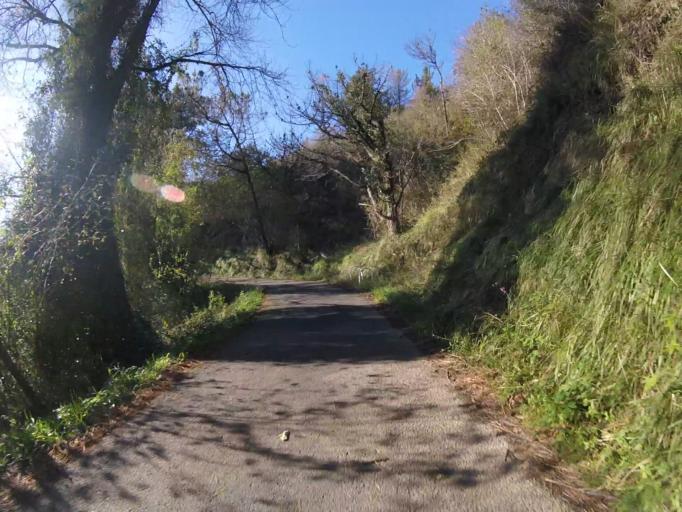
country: ES
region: Basque Country
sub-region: Provincia de Guipuzcoa
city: Usurbil
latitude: 43.2996
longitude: -2.0531
